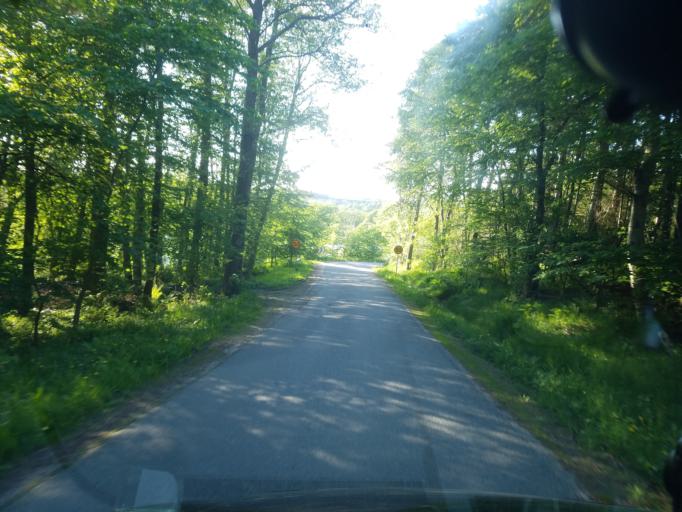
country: SE
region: Vaestra Goetaland
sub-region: Lysekils Kommun
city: Lysekil
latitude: 58.3048
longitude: 11.4615
